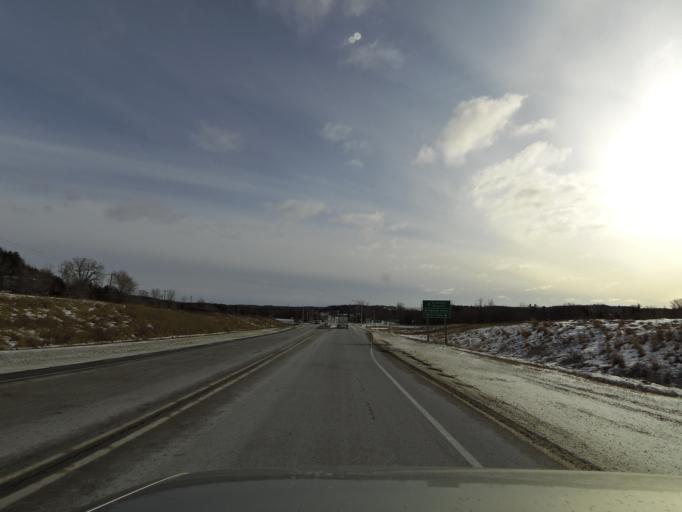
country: US
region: Wisconsin
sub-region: Pierce County
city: River Falls
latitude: 44.8523
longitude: -92.6061
